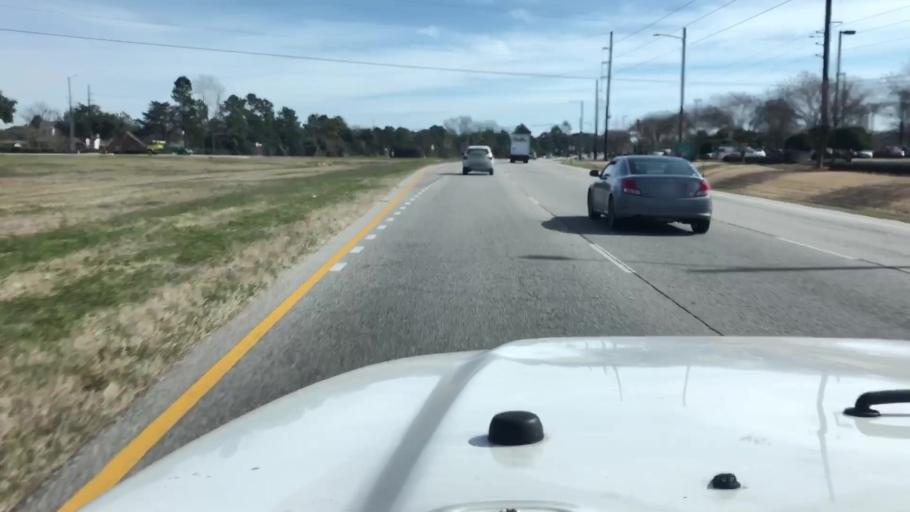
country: US
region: Alabama
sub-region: Elmore County
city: Blue Ridge
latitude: 32.3818
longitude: -86.1632
